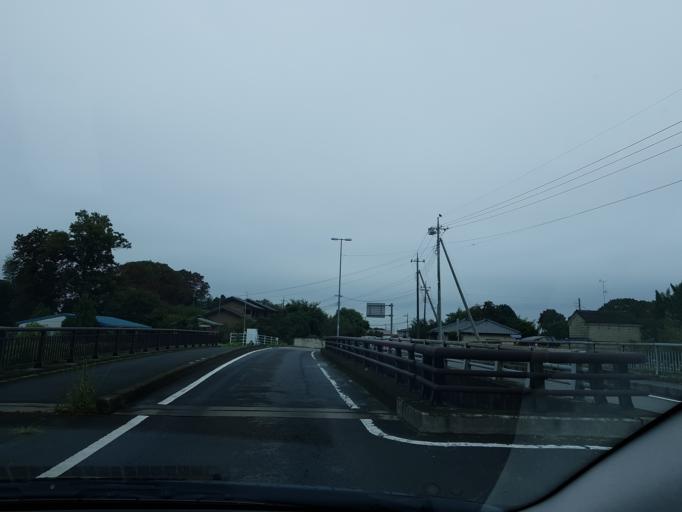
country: JP
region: Tochigi
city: Utsunomiya-shi
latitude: 36.5865
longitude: 139.8938
